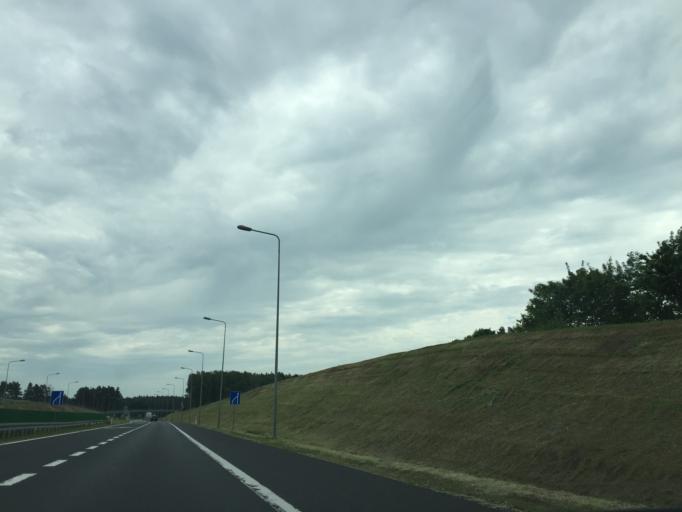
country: PL
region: Warmian-Masurian Voivodeship
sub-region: Powiat olsztynski
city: Czerwonka
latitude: 53.8281
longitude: 20.8252
